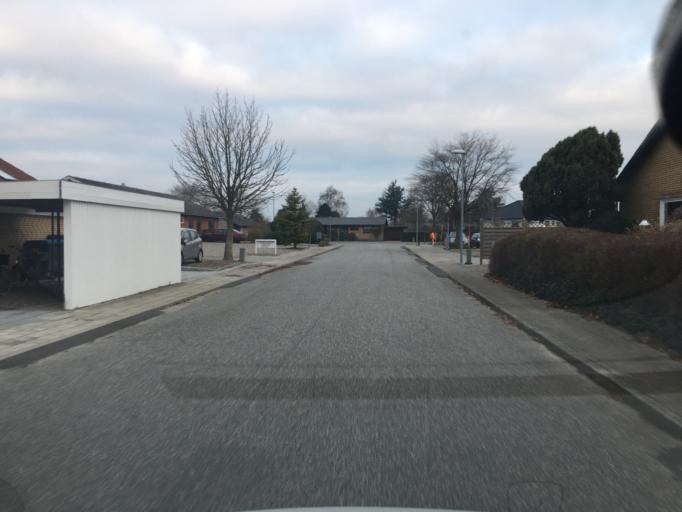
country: DK
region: South Denmark
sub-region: Tonder Kommune
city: Logumkloster
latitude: 55.0591
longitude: 8.9639
